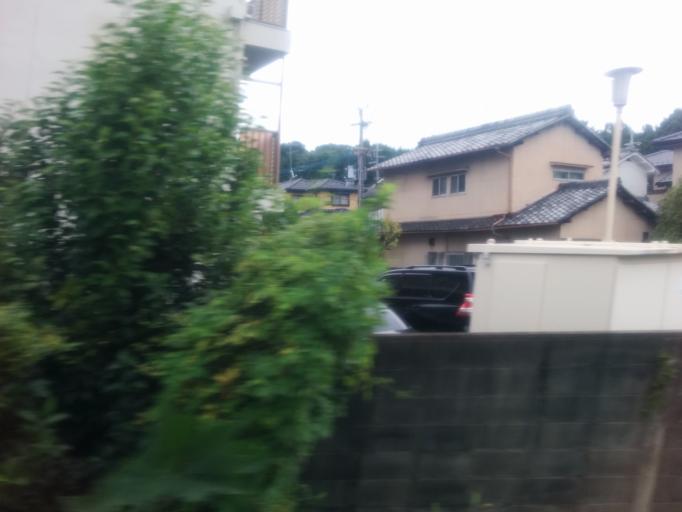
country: JP
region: Kyoto
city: Uji
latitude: 34.9428
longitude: 135.7721
